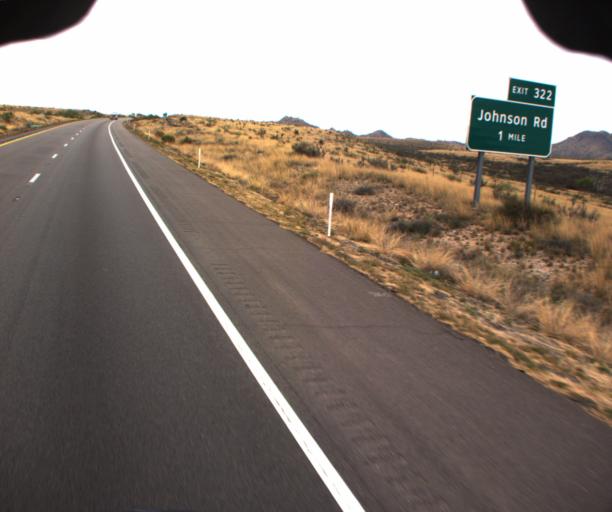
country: US
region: Arizona
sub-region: Cochise County
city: Willcox
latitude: 32.0933
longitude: -110.0365
